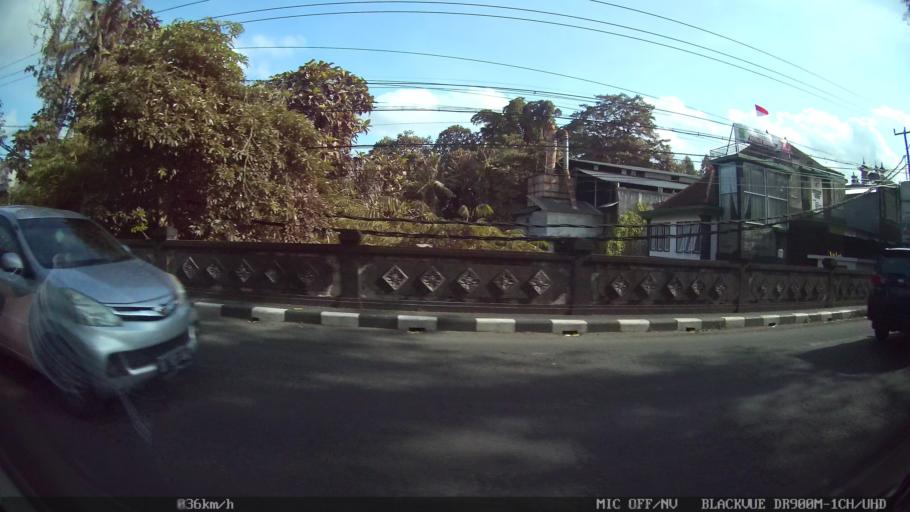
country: ID
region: Bali
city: Banjar Pekenjelodan
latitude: -8.5671
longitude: 115.1758
